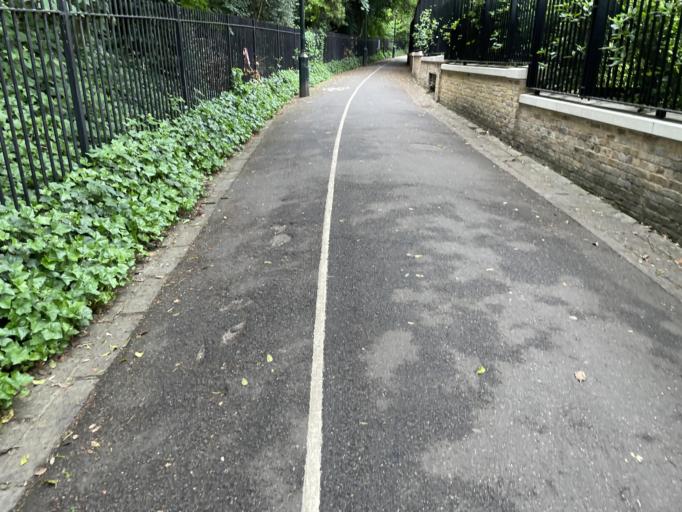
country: GB
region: England
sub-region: Greater London
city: Kensington
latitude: 51.5036
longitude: -0.2013
